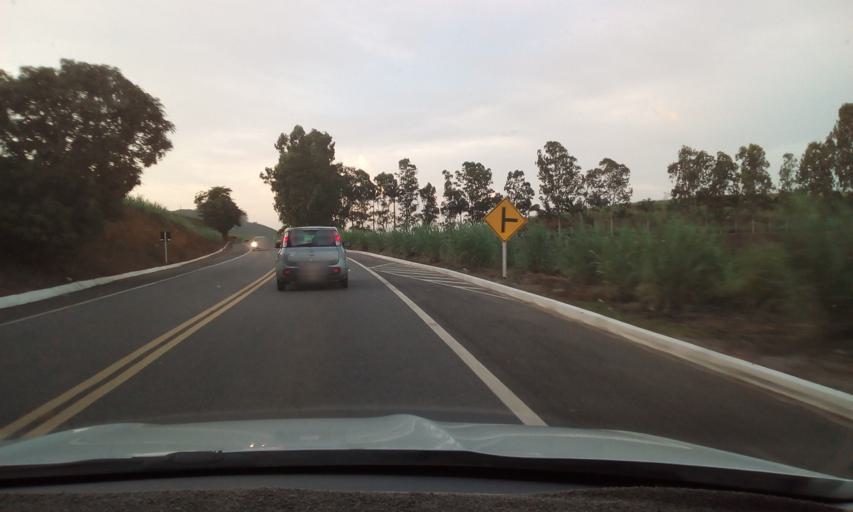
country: BR
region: Pernambuco
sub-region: Vicencia
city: Vicencia
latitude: -7.6012
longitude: -35.2415
